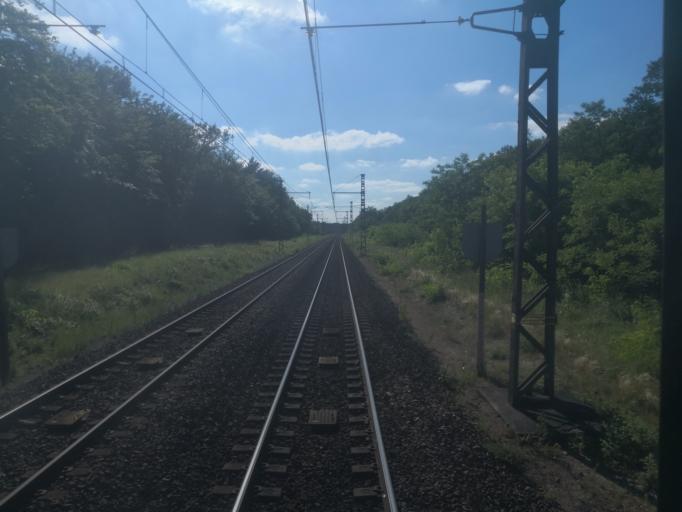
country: FR
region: Ile-de-France
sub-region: Departement de Seine-et-Marne
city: Thomery
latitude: 48.3949
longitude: 2.7580
